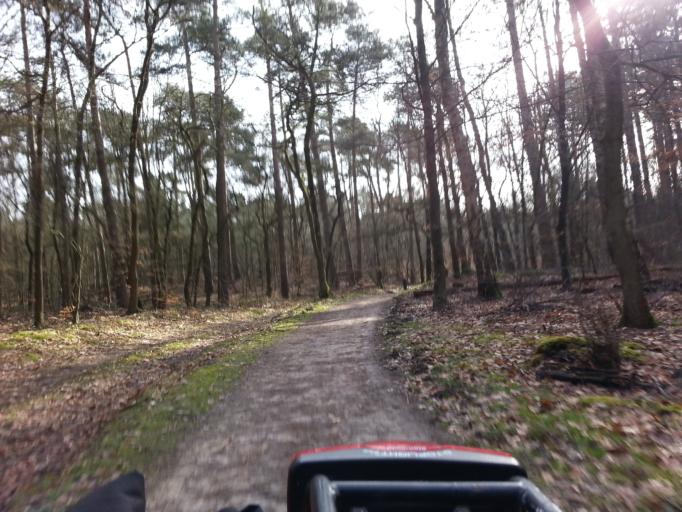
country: NL
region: Utrecht
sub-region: Gemeente Utrechtse Heuvelrug
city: Maarn
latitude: 52.0756
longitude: 5.3329
